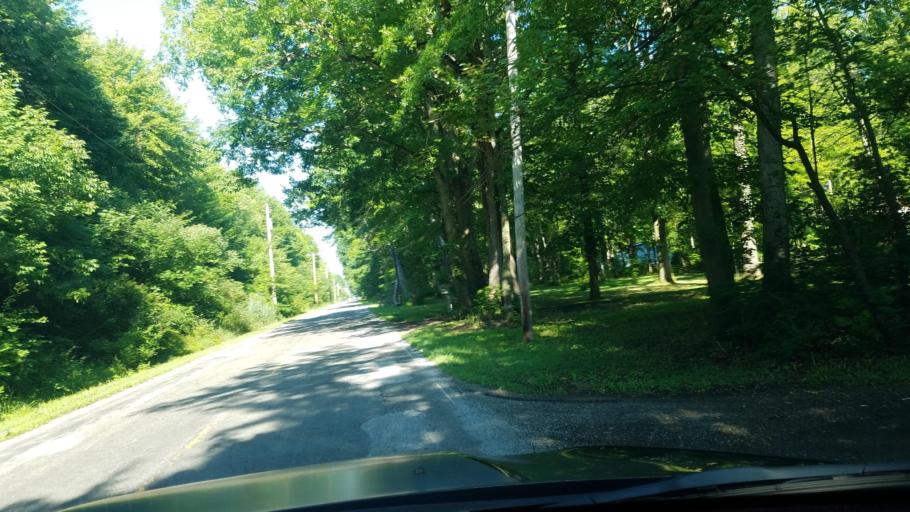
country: US
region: Ohio
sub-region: Trumbull County
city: Champion Heights
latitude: 41.3301
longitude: -80.7971
